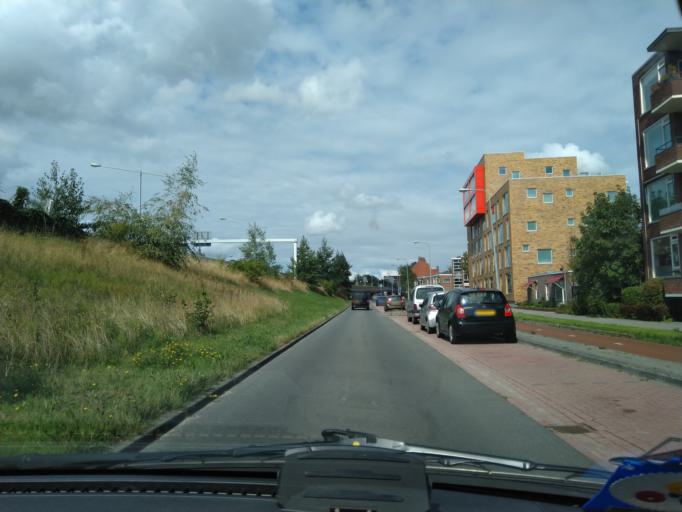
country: NL
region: Groningen
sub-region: Gemeente Groningen
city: Groningen
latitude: 53.2048
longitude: 6.5641
